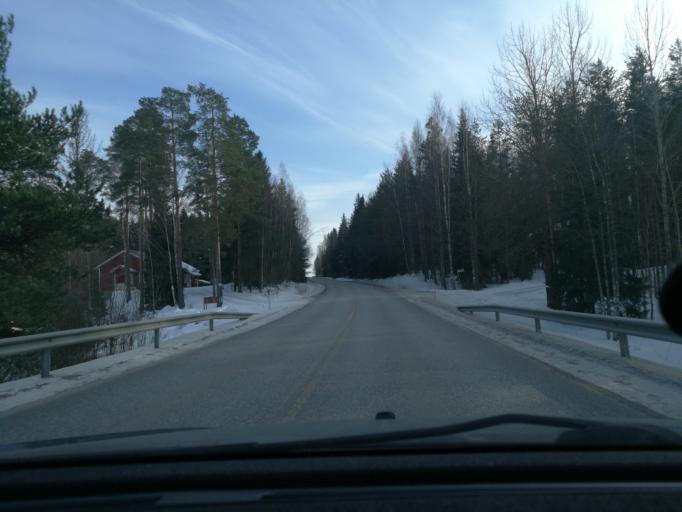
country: FI
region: Uusimaa
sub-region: Helsinki
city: Saukkola
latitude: 60.3895
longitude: 24.0775
